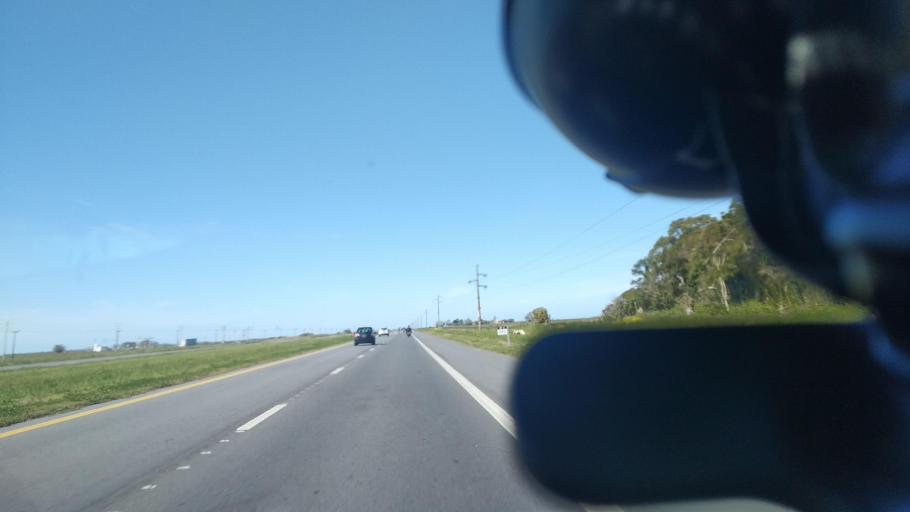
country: AR
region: Buenos Aires
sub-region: Partido de General Lavalle
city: General Lavalle
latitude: -36.4295
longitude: -56.8848
